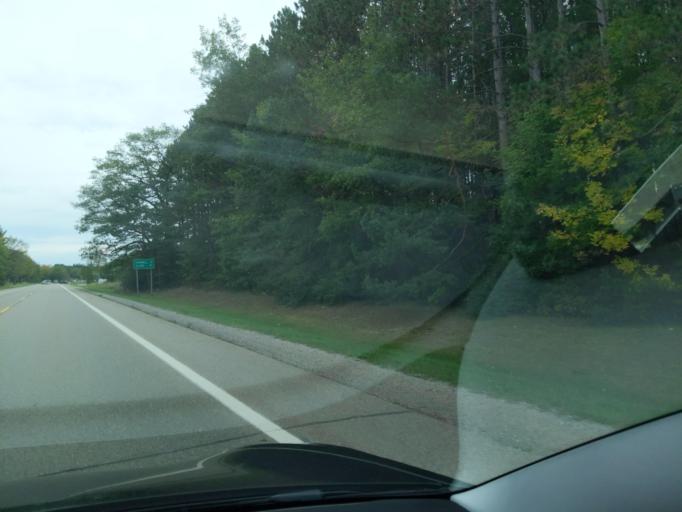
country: US
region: Michigan
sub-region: Clare County
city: Clare
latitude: 43.8619
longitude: -84.9059
